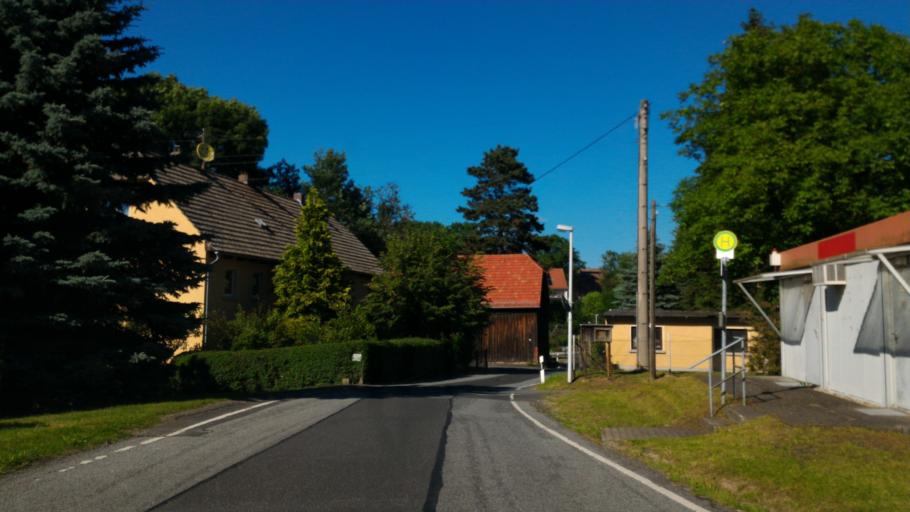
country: DE
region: Saxony
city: Mittelherwigsdorf
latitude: 50.9157
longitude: 14.7636
